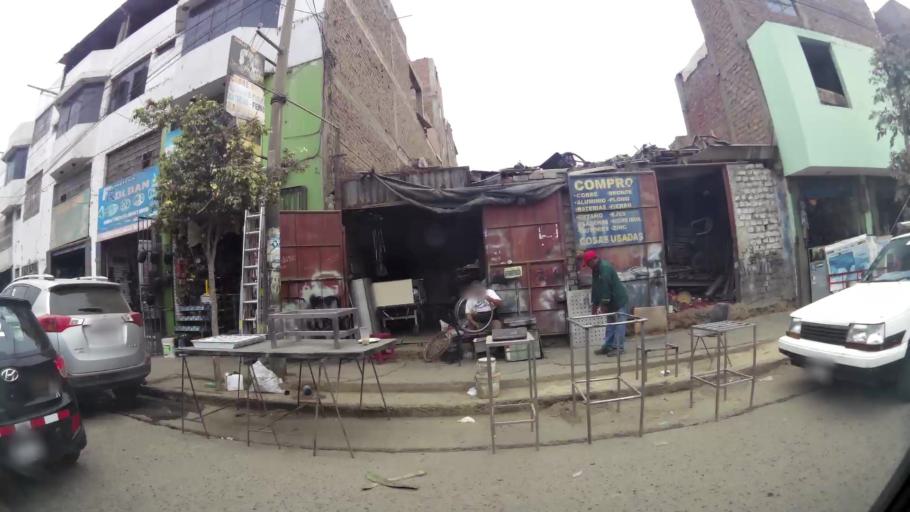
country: PE
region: La Libertad
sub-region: Provincia de Trujillo
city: Trujillo
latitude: -8.1137
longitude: -79.0178
